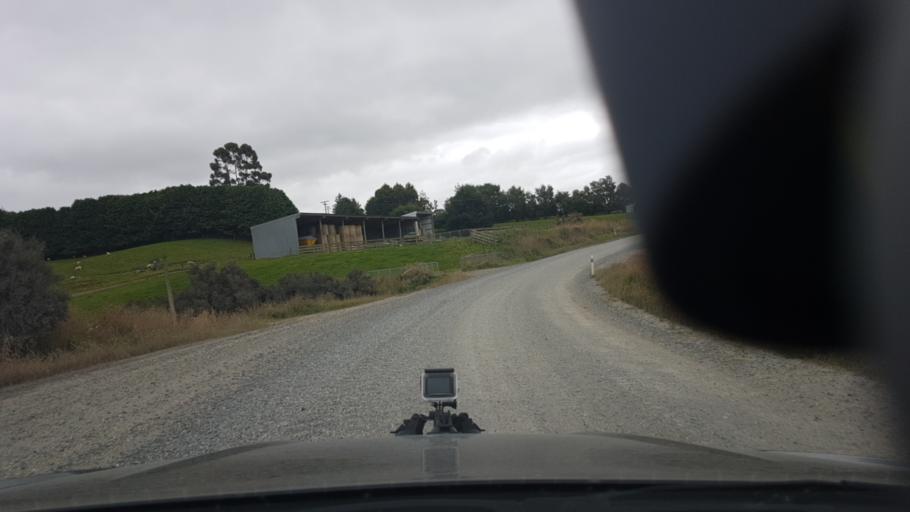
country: NZ
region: Otago
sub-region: Clutha District
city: Papatowai
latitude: -46.3230
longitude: 169.3747
